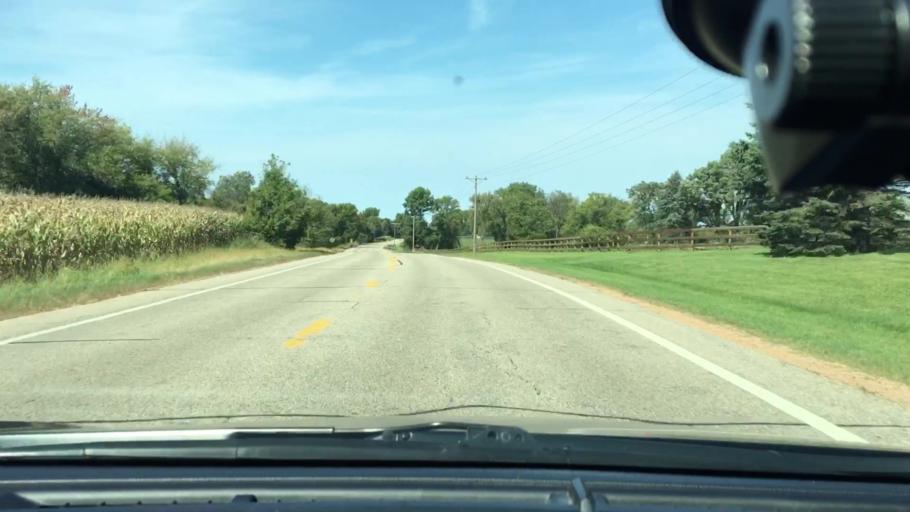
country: US
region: Minnesota
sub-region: Hennepin County
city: Corcoran
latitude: 45.1001
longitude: -93.5545
